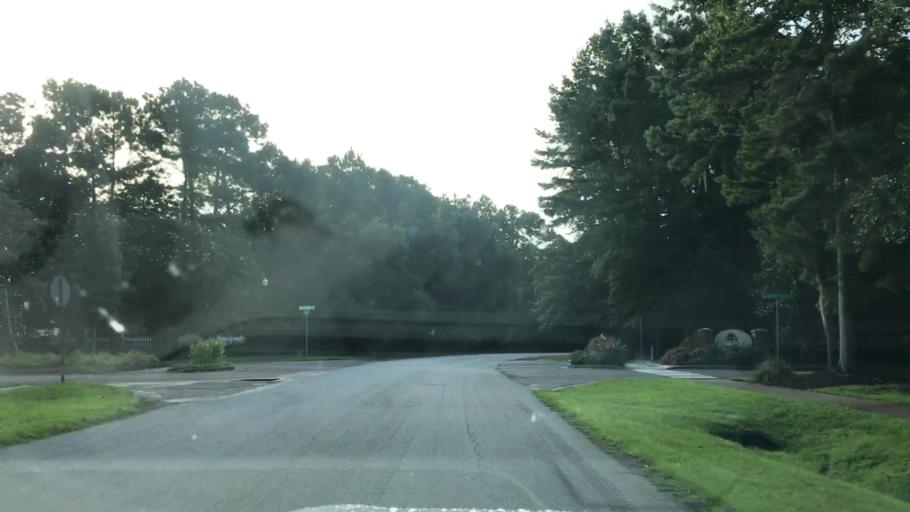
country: US
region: South Carolina
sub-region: Charleston County
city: Shell Point
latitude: 32.8411
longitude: -80.0879
